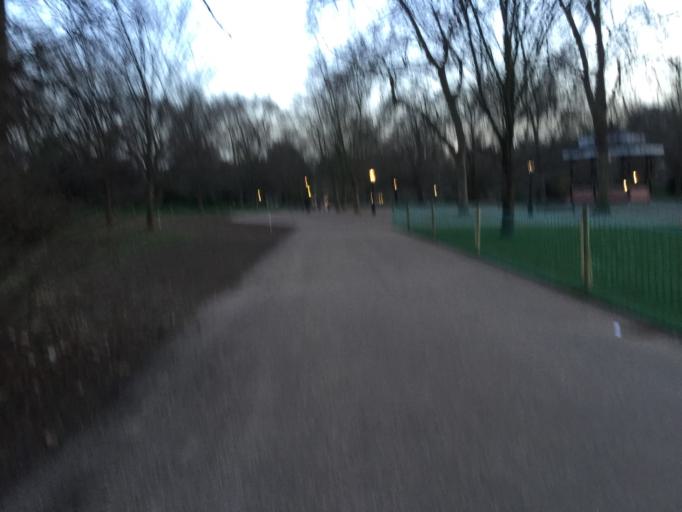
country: GB
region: England
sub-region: Greater London
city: Chelsea
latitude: 51.5057
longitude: -0.1560
